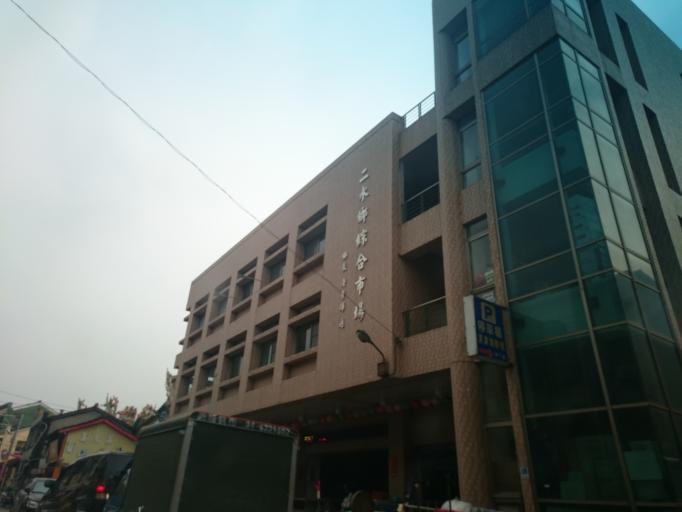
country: TW
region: Taiwan
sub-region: Nantou
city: Nantou
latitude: 23.8105
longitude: 120.6156
